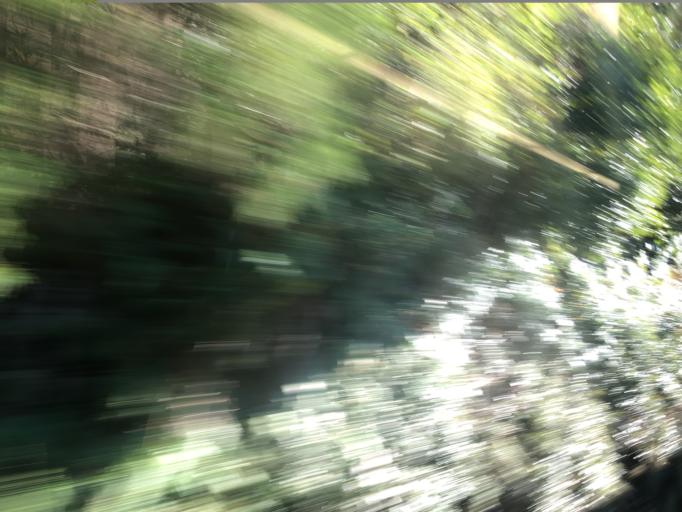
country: JP
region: Kochi
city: Nakamura
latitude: 33.0114
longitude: 132.9900
